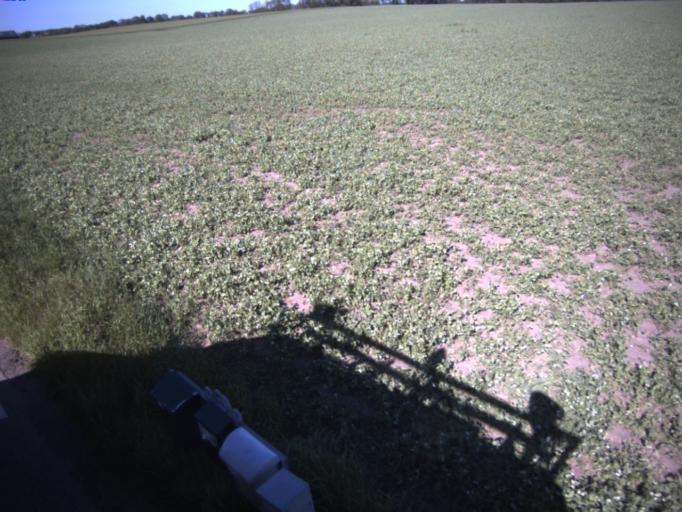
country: SE
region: Skane
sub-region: Helsingborg
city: Gantofta
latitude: 55.9789
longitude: 12.8126
